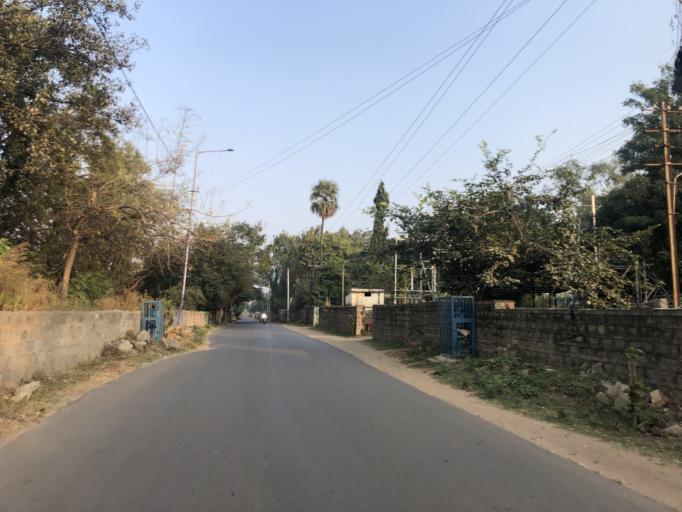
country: IN
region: Telangana
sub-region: Rangareddi
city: Kukatpalli
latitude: 17.4626
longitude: 78.4377
